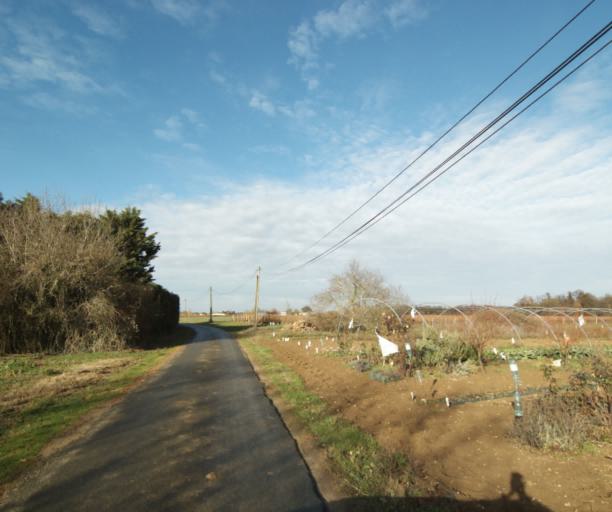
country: FR
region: Poitou-Charentes
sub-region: Departement de la Charente-Maritime
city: Meursac
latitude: 45.6905
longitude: -0.7922
